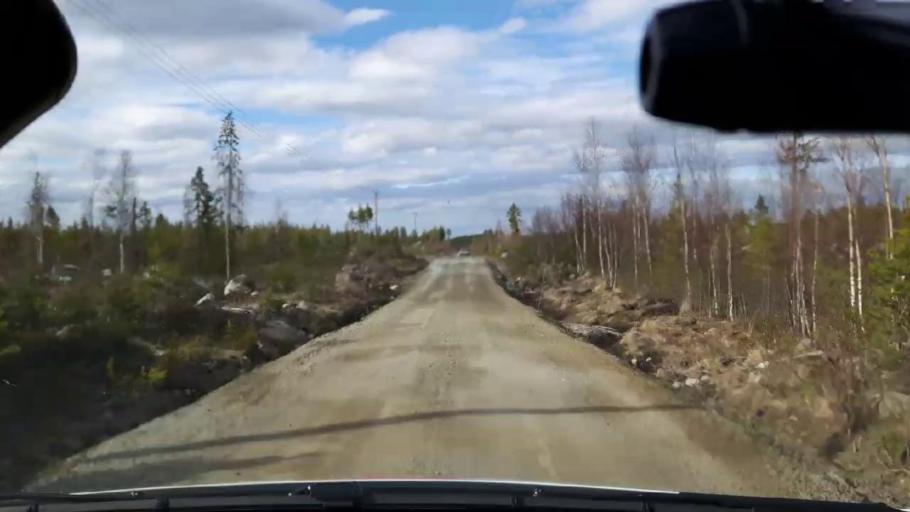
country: SE
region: Jaemtland
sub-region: Bergs Kommun
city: Hoverberg
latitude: 62.8398
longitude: 14.6667
